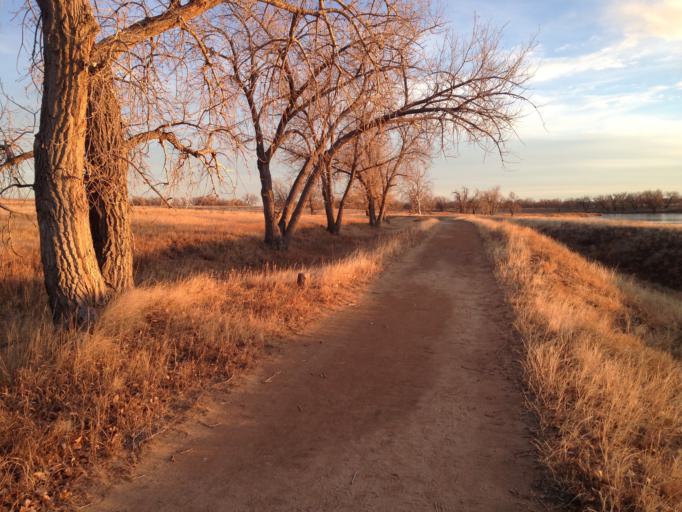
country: US
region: Colorado
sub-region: Adams County
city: Derby
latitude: 39.8184
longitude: -104.8562
